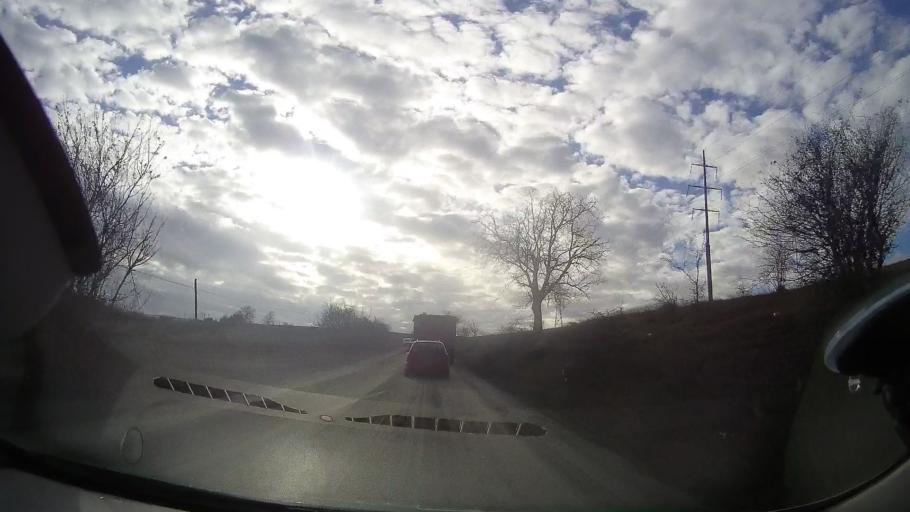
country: RO
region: Cluj
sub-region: Comuna Savadisla
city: Savadisla
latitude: 46.6552
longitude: 23.4520
